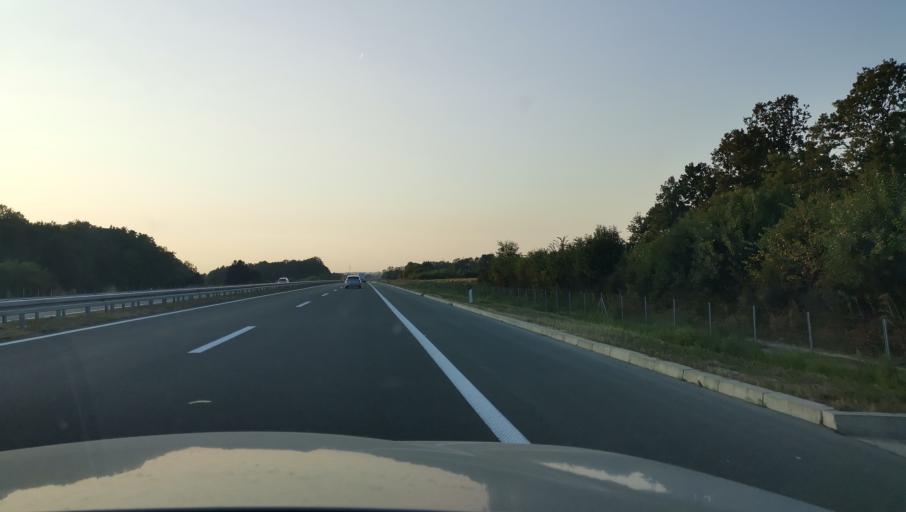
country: RS
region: Central Serbia
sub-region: Kolubarski Okrug
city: Lajkovac
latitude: 44.3873
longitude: 20.1074
